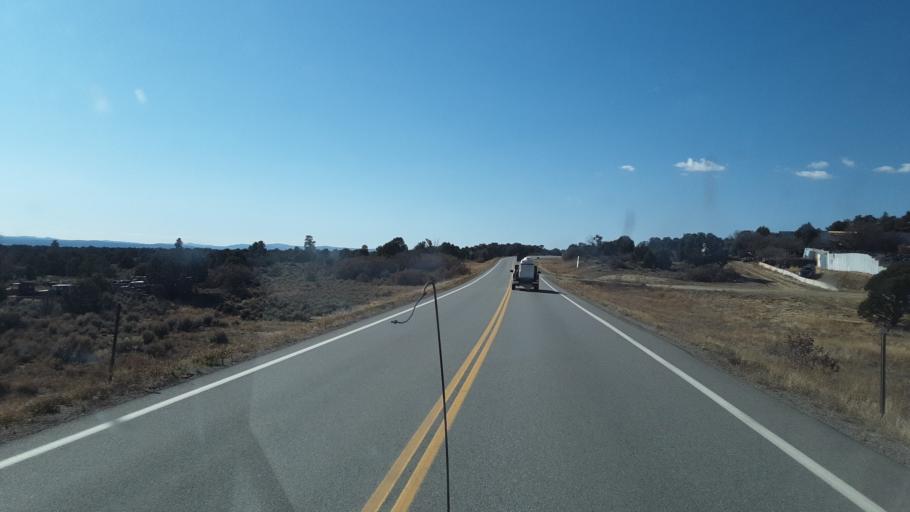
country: US
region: Colorado
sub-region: La Plata County
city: Bayfield
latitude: 37.2264
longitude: -107.6971
